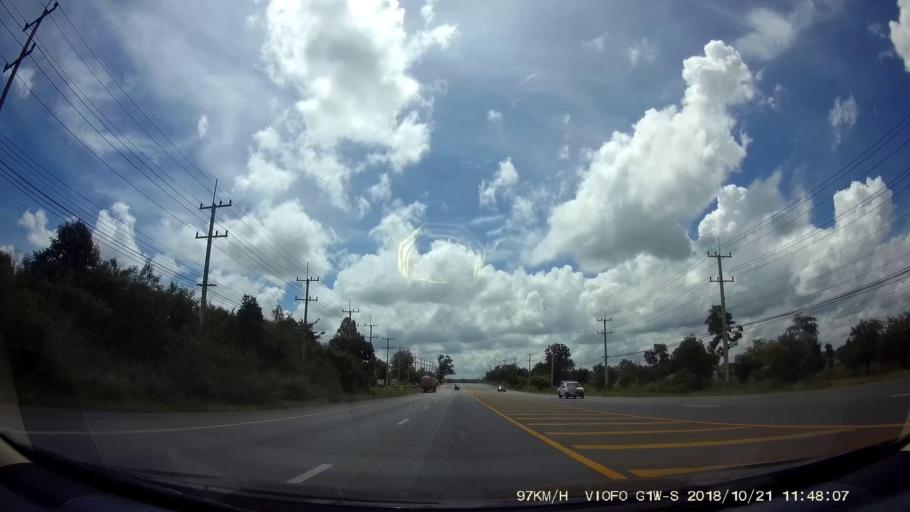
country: TH
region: Chaiyaphum
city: Noen Sa-nga
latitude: 15.6520
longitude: 101.9510
